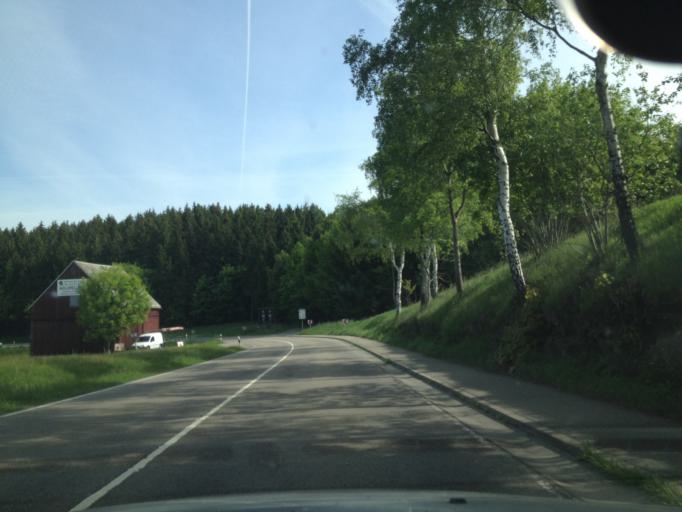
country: DE
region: Saxony
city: Annaberg-Buchholz
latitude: 50.5691
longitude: 13.0128
